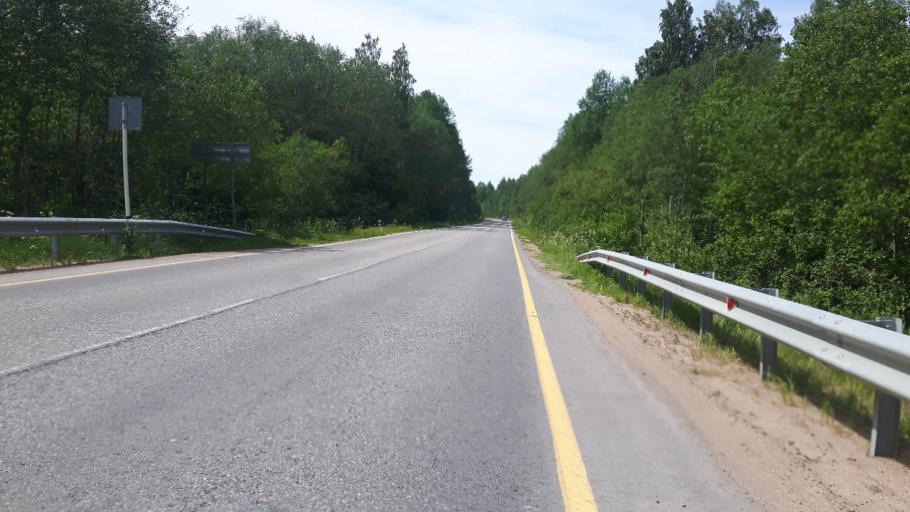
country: RU
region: Leningrad
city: Ust'-Luga
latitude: 59.6466
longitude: 28.2091
